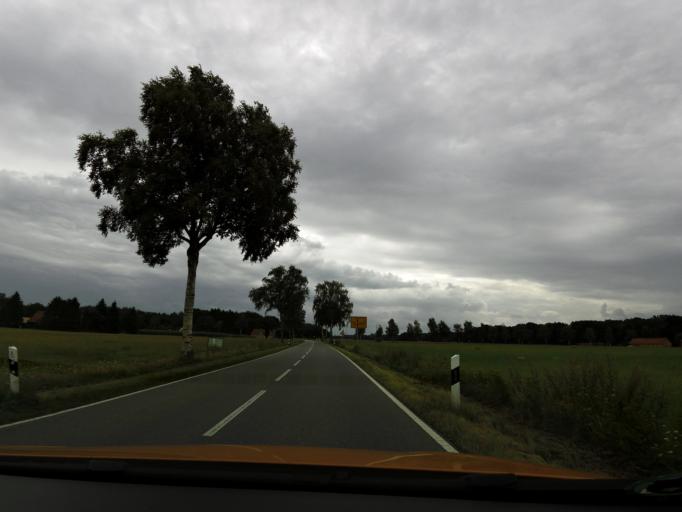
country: DE
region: Lower Saxony
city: Dunsen
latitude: 52.8888
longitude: 8.6224
